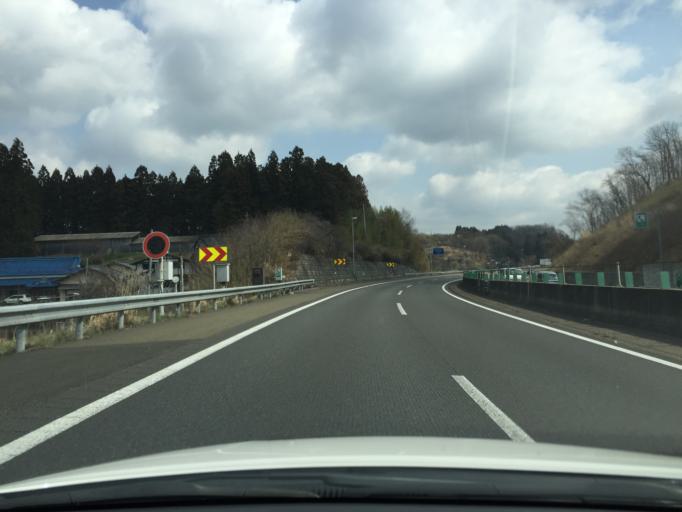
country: JP
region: Miyagi
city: Iwanuma
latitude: 38.1842
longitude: 140.7683
